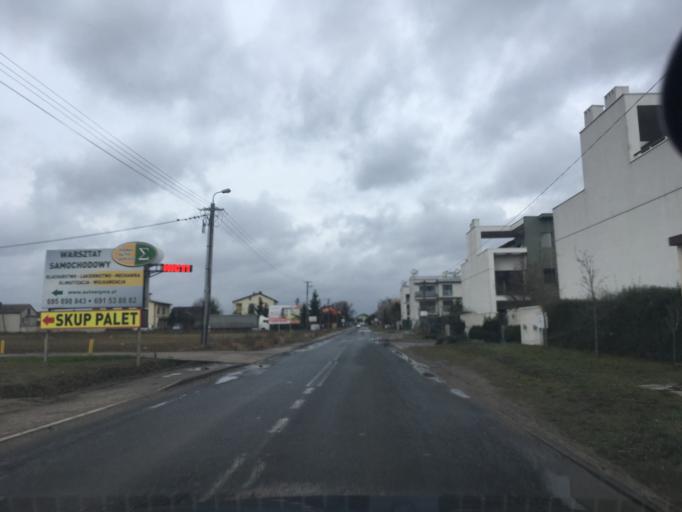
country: PL
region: Masovian Voivodeship
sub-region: Powiat piaseczynski
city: Lesznowola
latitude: 52.1017
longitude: 20.9322
